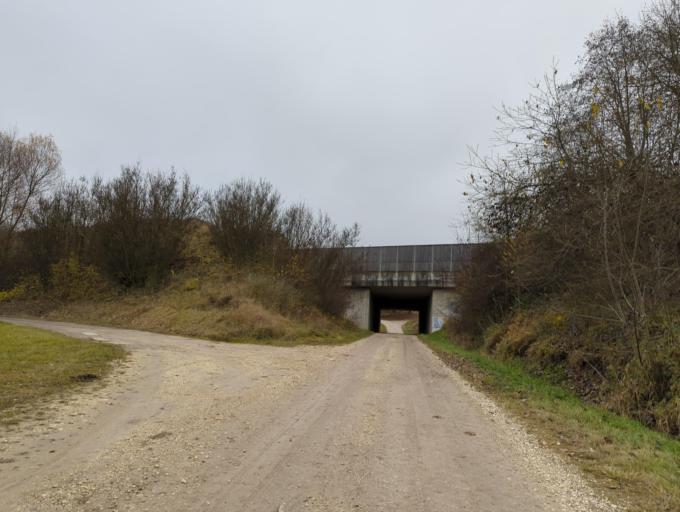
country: DE
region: Bavaria
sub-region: Swabia
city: Rettenbach
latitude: 48.4374
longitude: 10.3242
